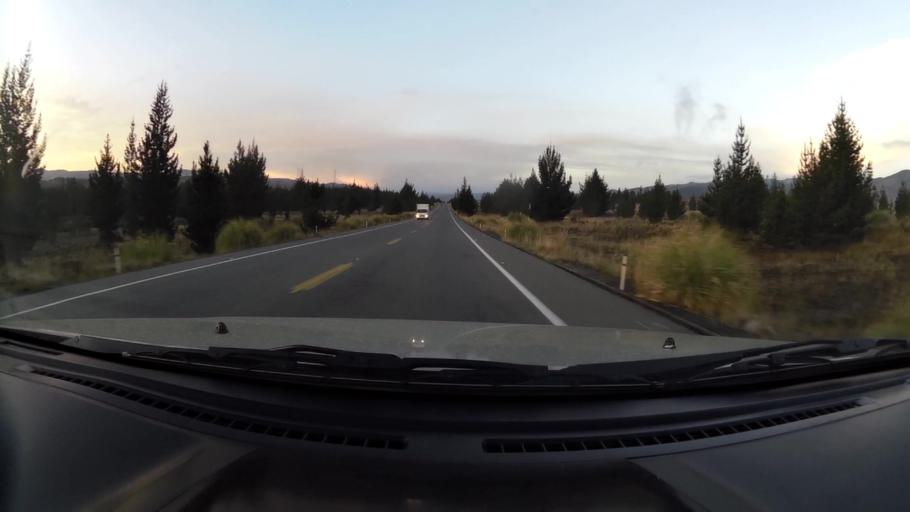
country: EC
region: Chimborazo
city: Alausi
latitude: -2.0341
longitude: -78.7360
